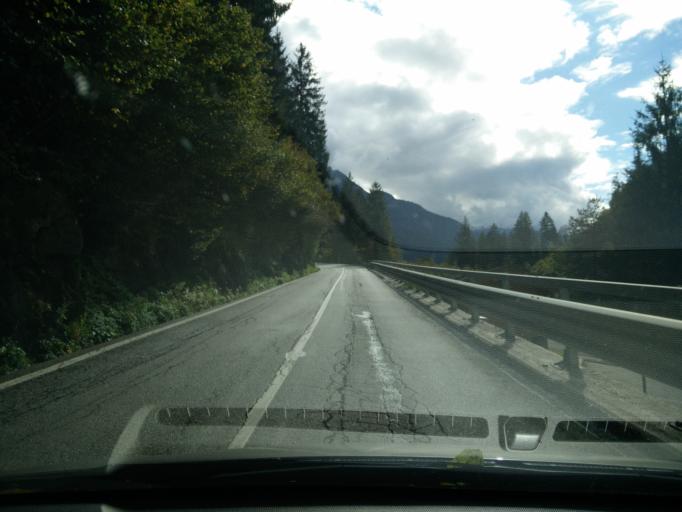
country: IT
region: Veneto
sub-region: Provincia di Belluno
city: Lozzo di Cadore
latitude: 46.4940
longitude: 12.4525
